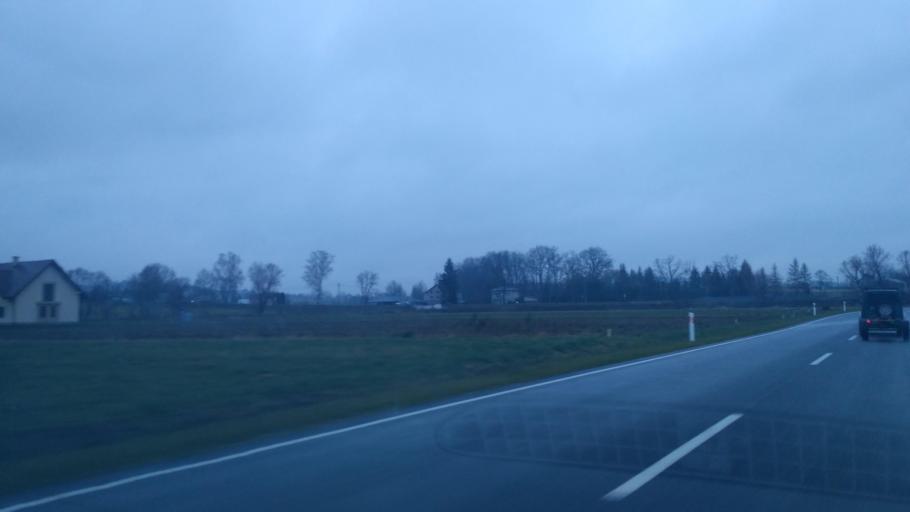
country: PL
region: Subcarpathian Voivodeship
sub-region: Powiat rzeszowski
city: Dynow
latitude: 49.8318
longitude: 22.2417
